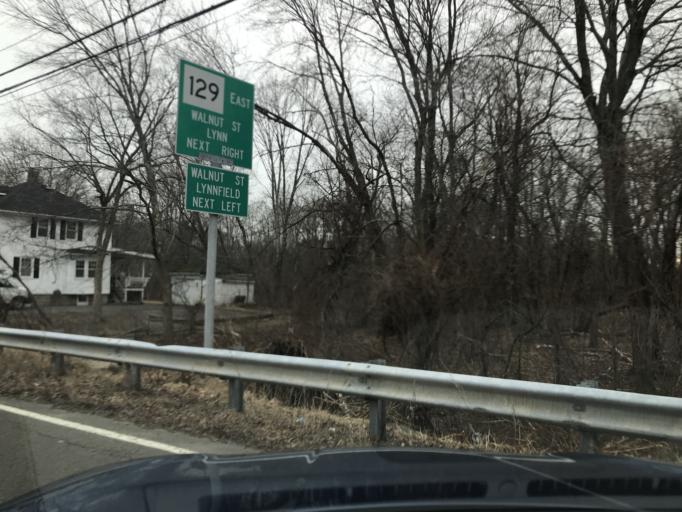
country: US
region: Massachusetts
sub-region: Essex County
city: Saugus
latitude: 42.4948
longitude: -71.0217
